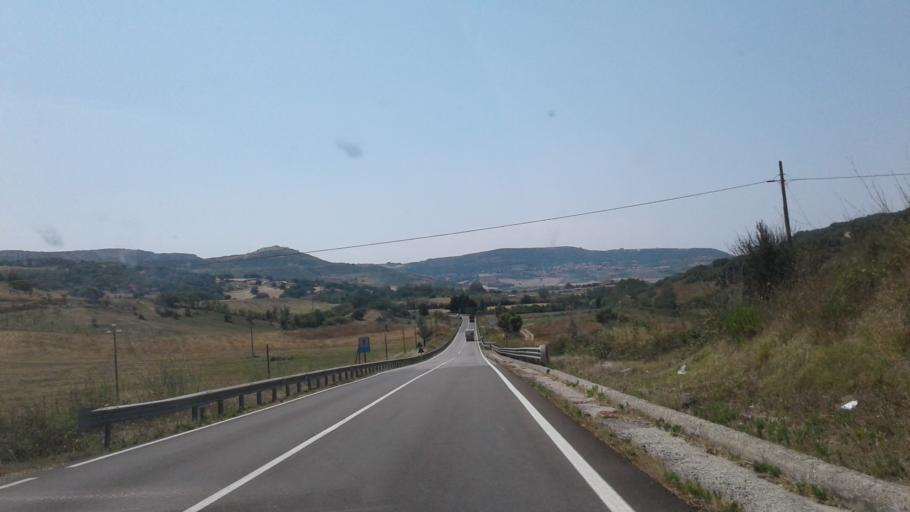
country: IT
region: Sardinia
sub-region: Provincia di Sassari
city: Codrongianos
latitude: 40.6716
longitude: 8.6777
